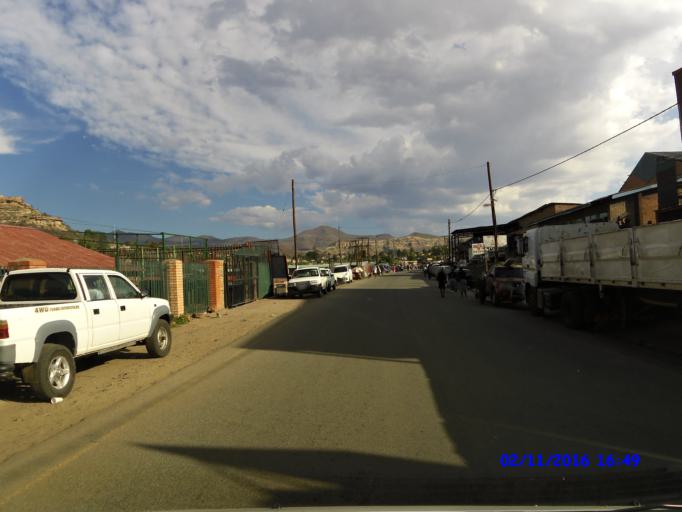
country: LS
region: Butha-Buthe
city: Butha-Buthe
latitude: -28.7649
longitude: 28.2515
